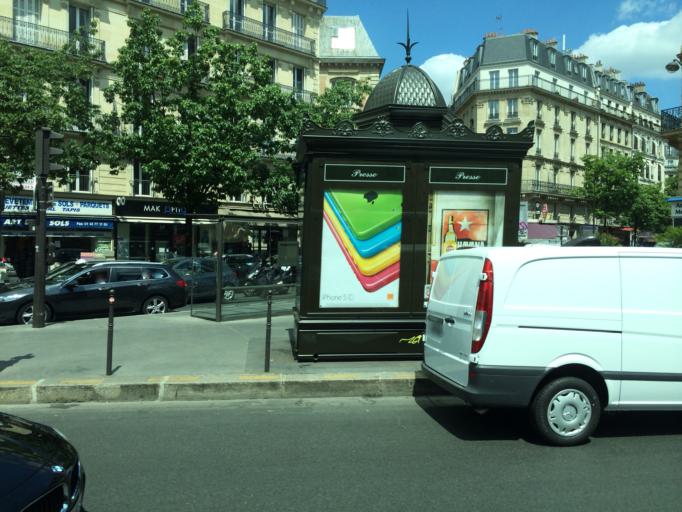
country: FR
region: Ile-de-France
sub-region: Paris
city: Paris
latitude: 48.8654
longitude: 2.3563
